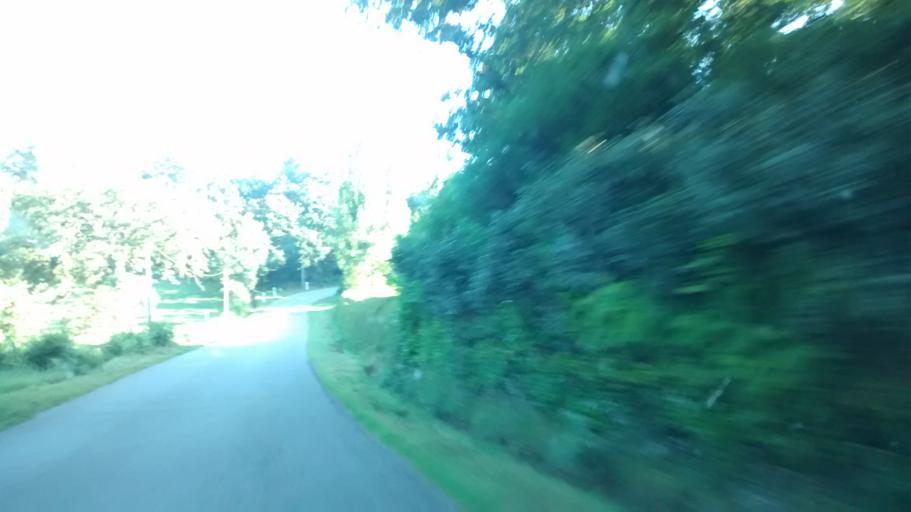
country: FR
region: Brittany
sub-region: Departement du Morbihan
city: Campeneac
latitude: 47.9787
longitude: -2.3096
